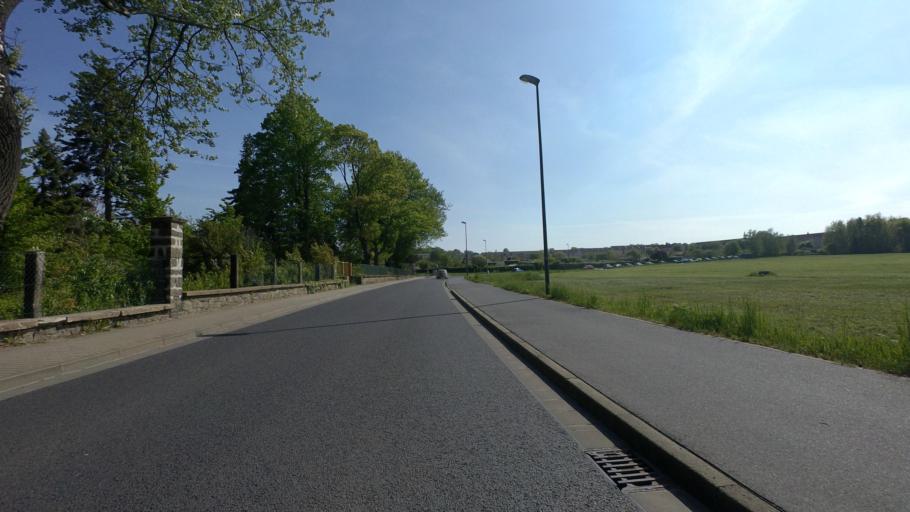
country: DE
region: Saxony
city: Kamenz
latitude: 51.2771
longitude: 14.1144
